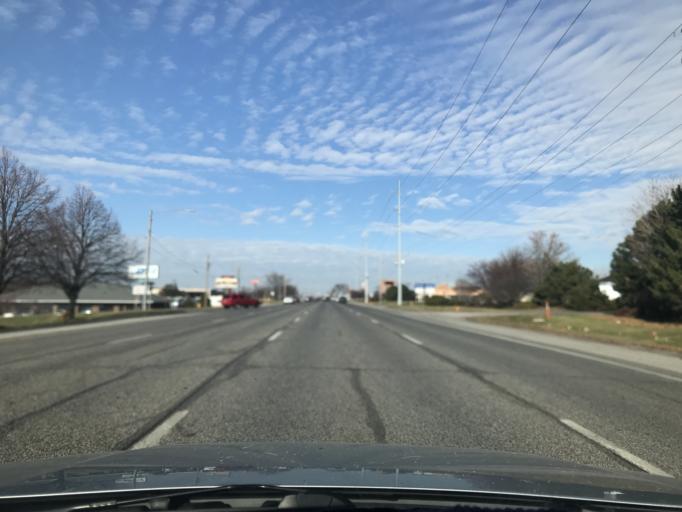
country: US
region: Iowa
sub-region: Scott County
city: Davenport
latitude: 41.5706
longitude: -90.5686
